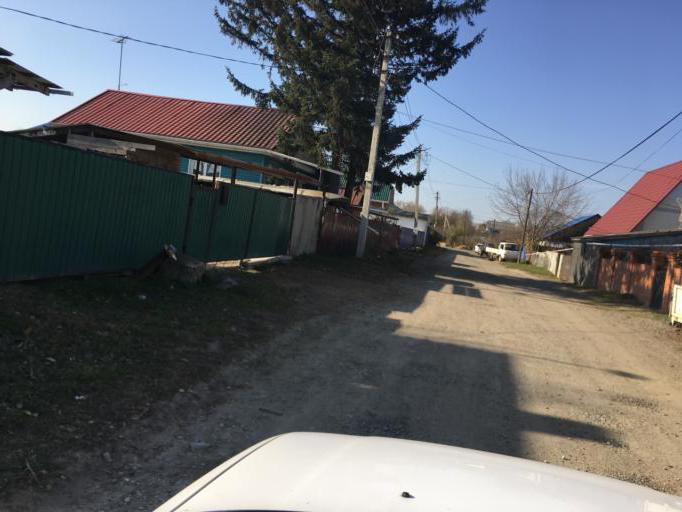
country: RU
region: Primorskiy
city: Dal'nerechensk
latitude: 45.9236
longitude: 133.7278
